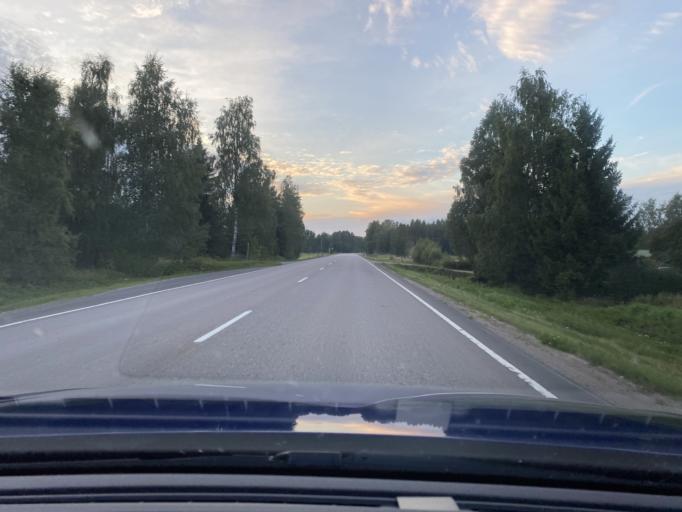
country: FI
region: Satakunta
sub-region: Pohjois-Satakunta
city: Honkajoki
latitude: 61.8878
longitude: 22.2887
